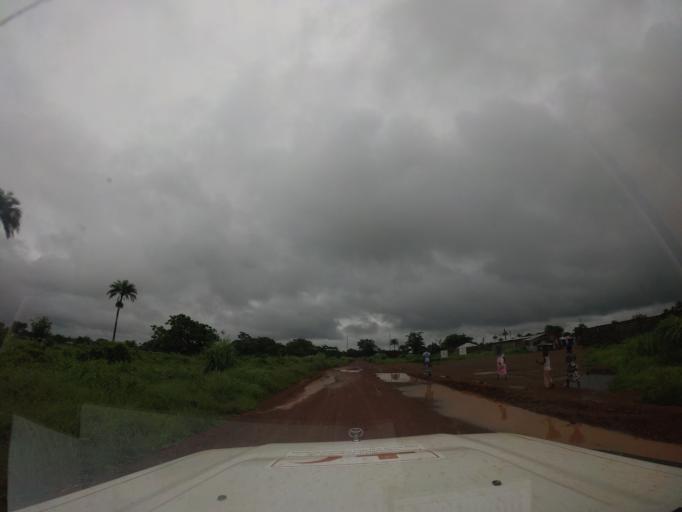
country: SL
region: Northern Province
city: Kambia
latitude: 9.1287
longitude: -12.9045
